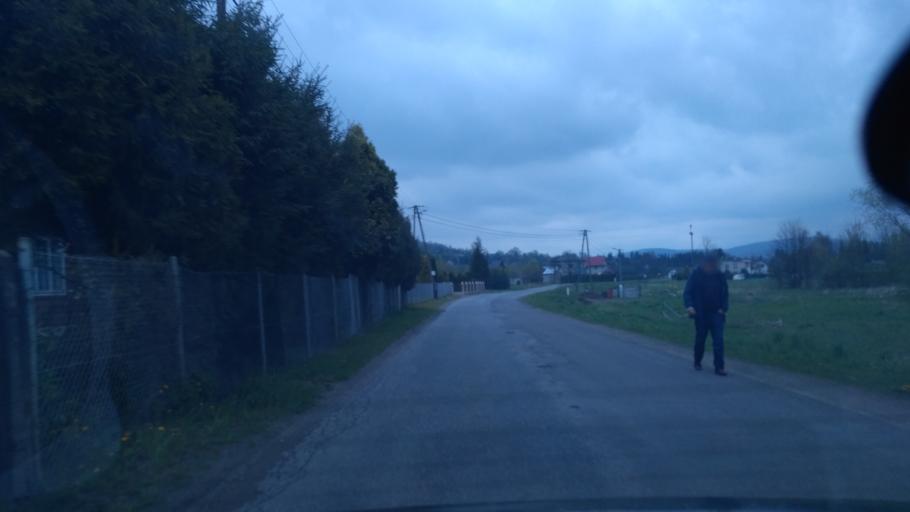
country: PL
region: Subcarpathian Voivodeship
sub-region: Powiat sanocki
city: Sanok
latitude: 49.6220
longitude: 22.2739
